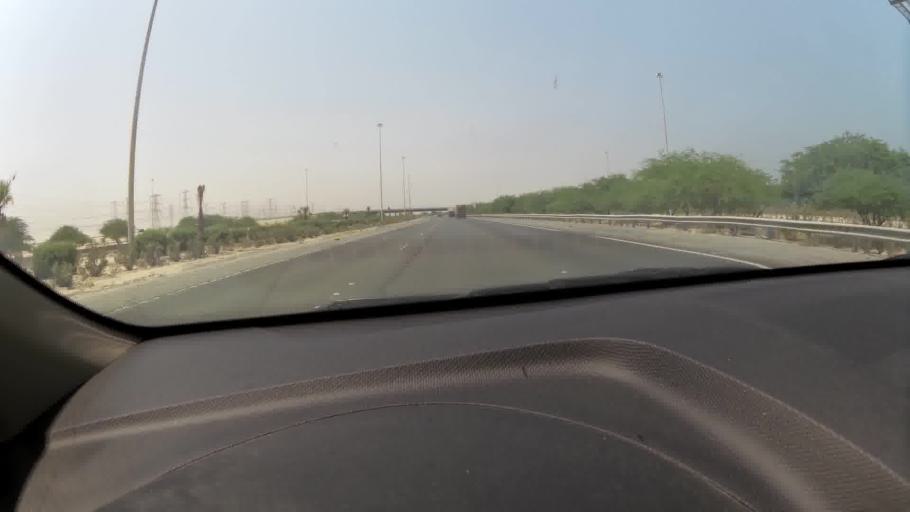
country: KW
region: Al Ahmadi
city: Al Fahahil
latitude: 28.9173
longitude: 48.2078
